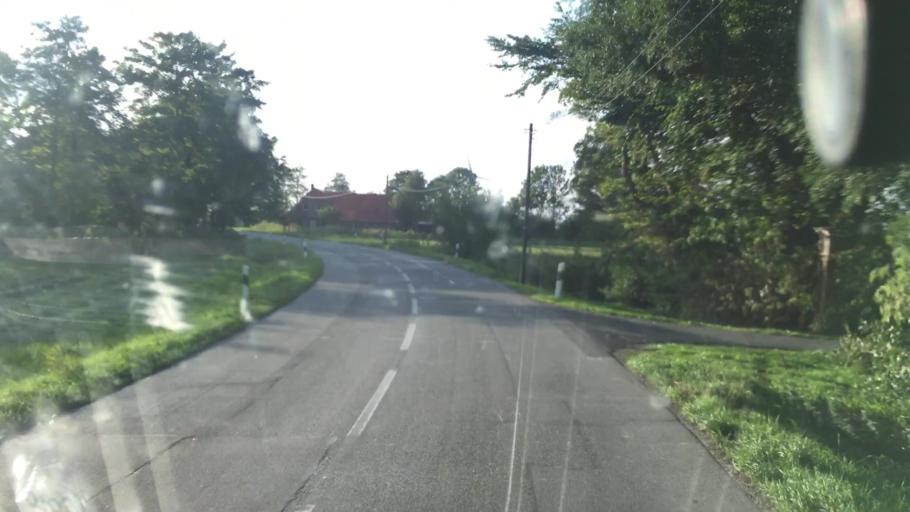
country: DE
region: Lower Saxony
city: Werdum
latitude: 53.6593
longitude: 7.7741
